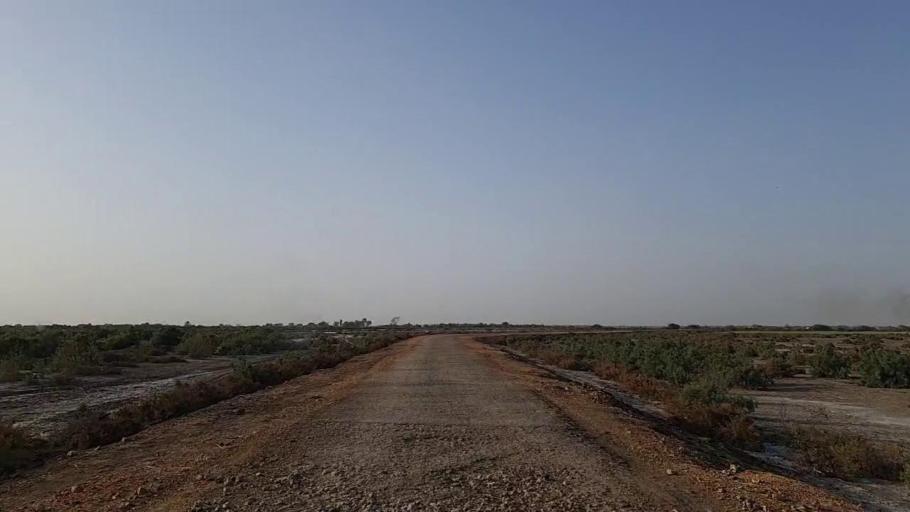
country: PK
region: Sindh
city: Jati
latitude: 24.3627
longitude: 68.1455
